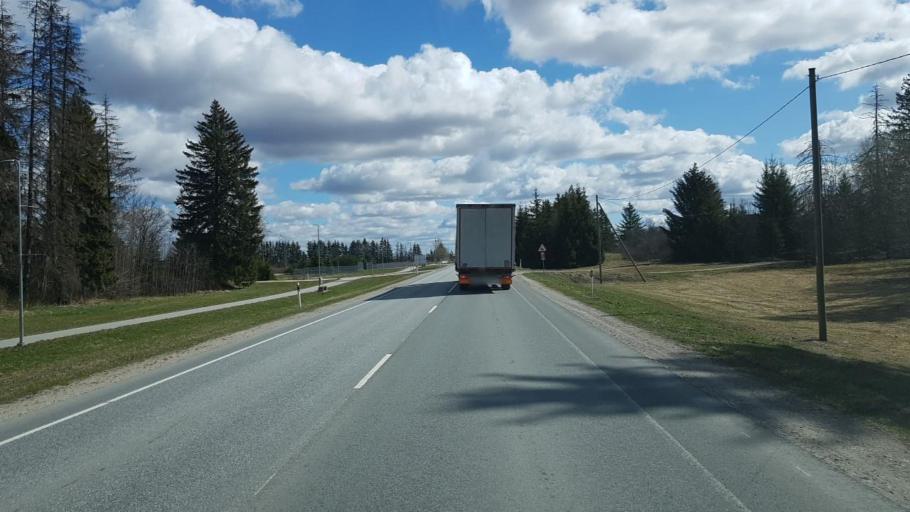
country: EE
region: Laeaene-Virumaa
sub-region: Tapa vald
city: Tapa
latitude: 59.2533
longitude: 25.9809
